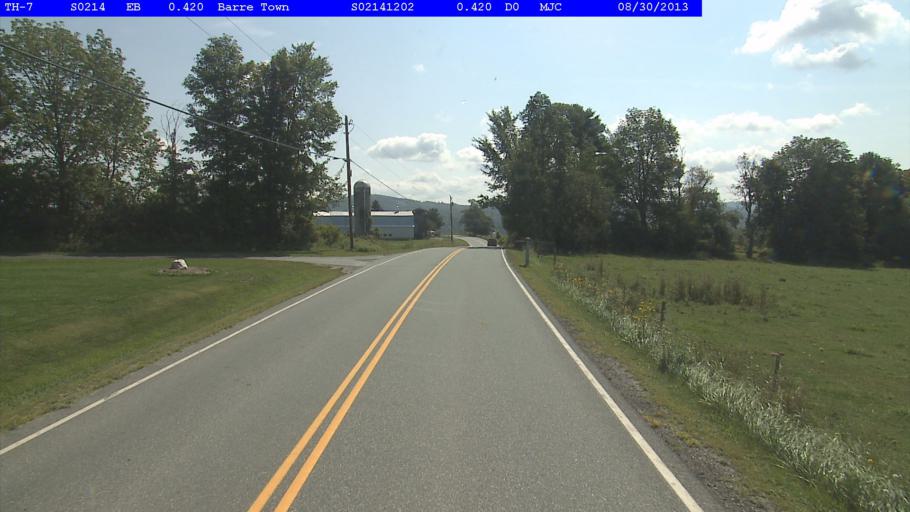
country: US
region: Vermont
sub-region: Washington County
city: South Barre
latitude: 44.1849
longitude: -72.5192
